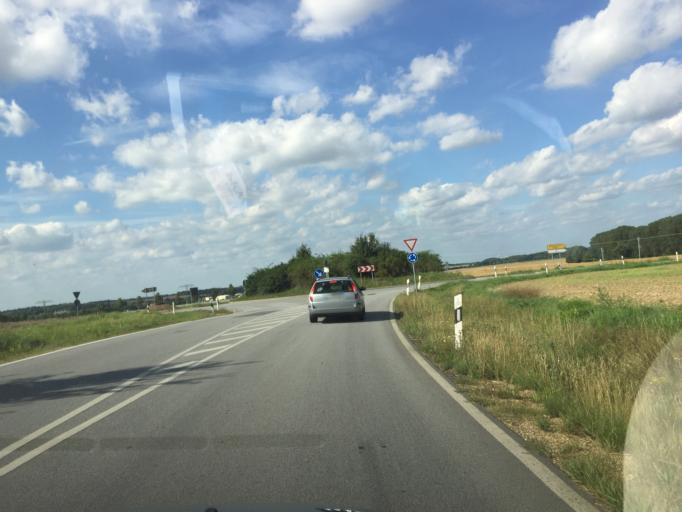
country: DE
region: Saxony
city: Kubschutz
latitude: 51.1810
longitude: 14.4852
